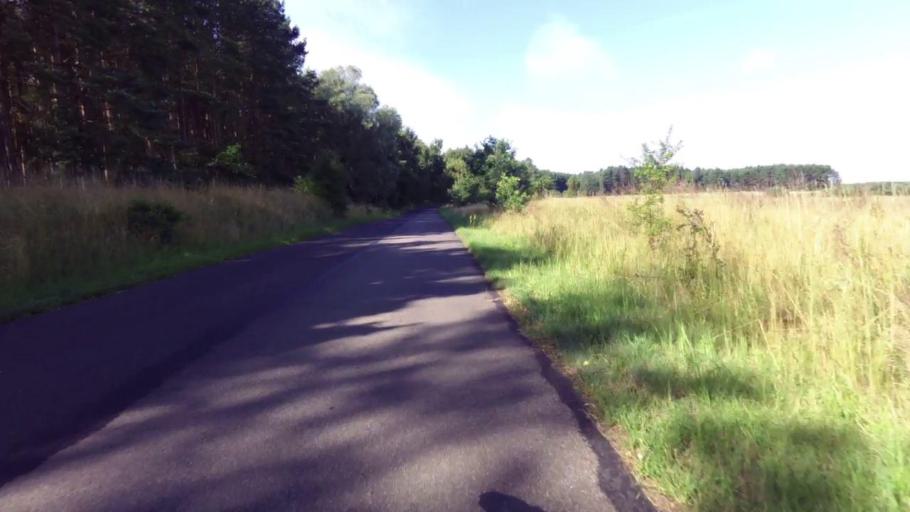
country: PL
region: West Pomeranian Voivodeship
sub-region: Powiat stargardzki
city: Marianowo
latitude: 53.3745
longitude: 15.2593
